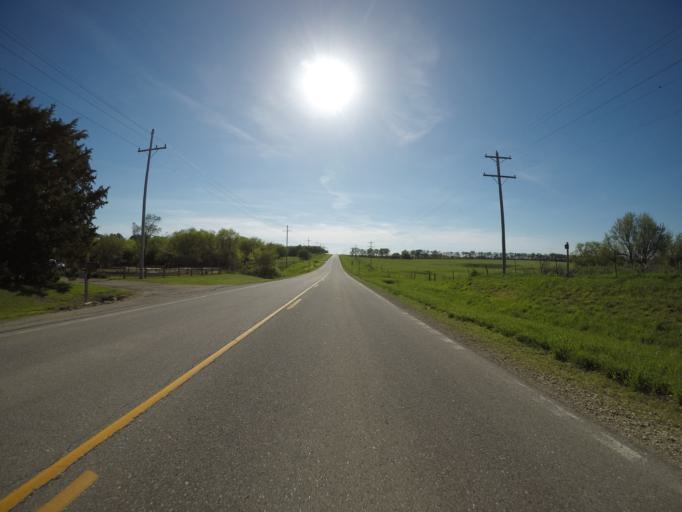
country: US
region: Kansas
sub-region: Clay County
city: Clay Center
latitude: 39.3646
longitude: -96.8732
